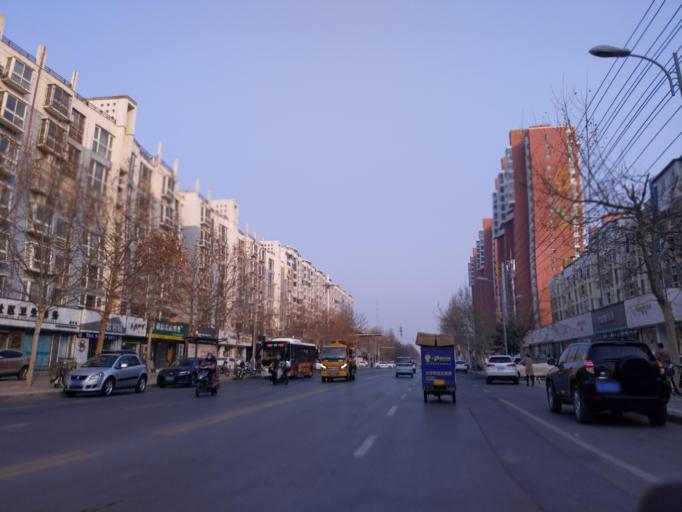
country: CN
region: Henan Sheng
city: Zhongyuanlu
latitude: 35.7740
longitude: 115.0633
